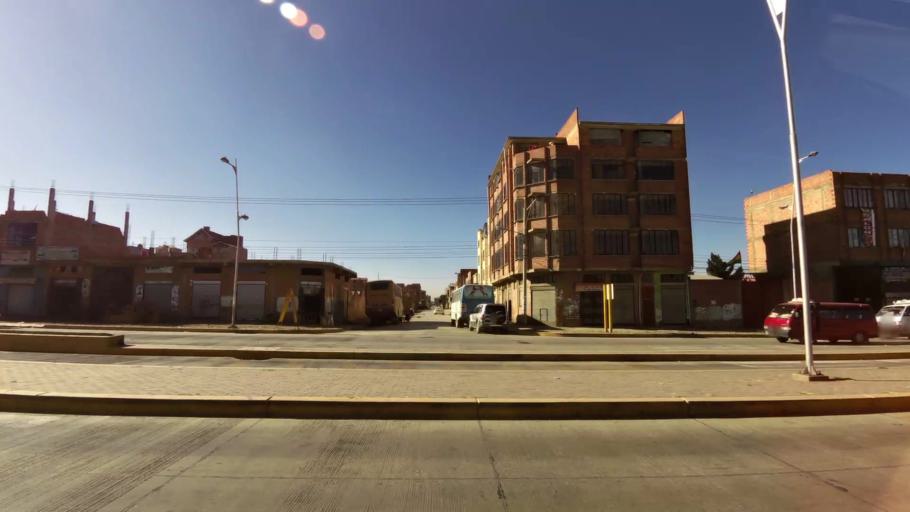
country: BO
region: La Paz
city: La Paz
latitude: -16.5266
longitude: -68.1835
